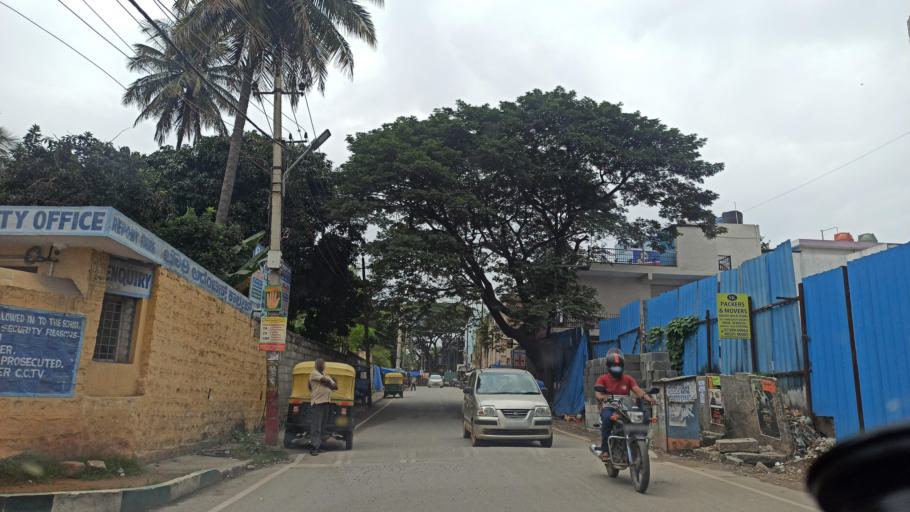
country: IN
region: Karnataka
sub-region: Bangalore Urban
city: Bangalore
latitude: 12.9995
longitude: 77.6767
